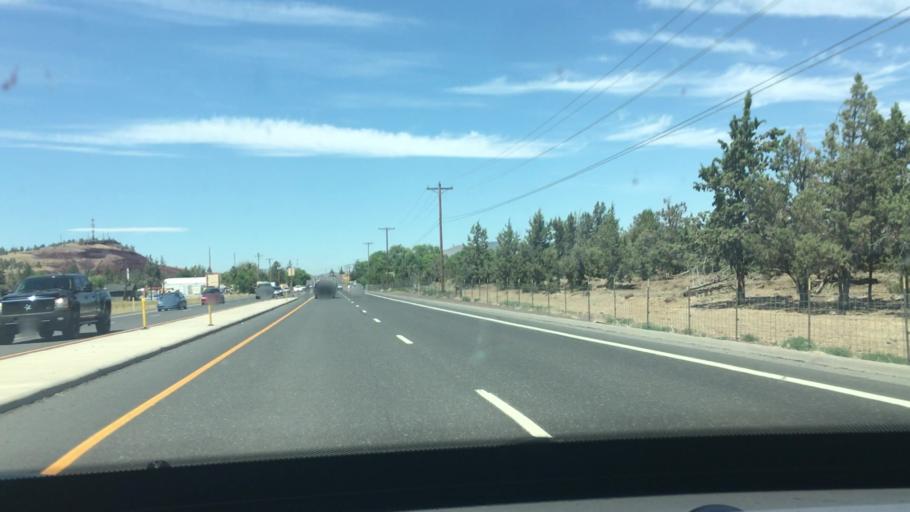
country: US
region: Oregon
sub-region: Deschutes County
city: Redmond
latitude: 44.3069
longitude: -121.1726
